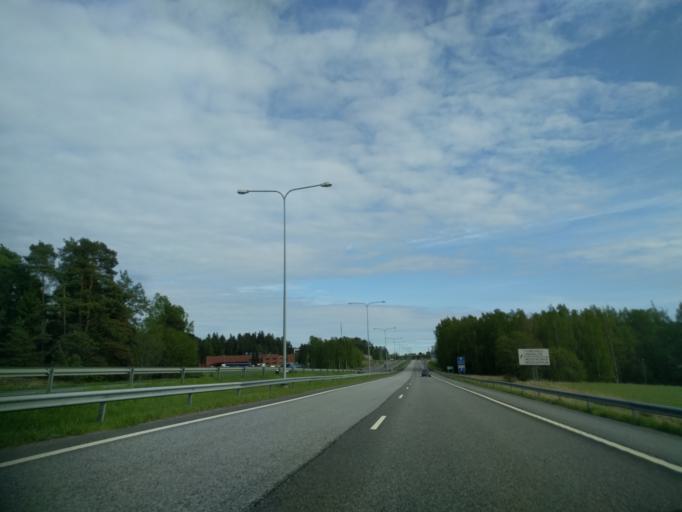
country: FI
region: Varsinais-Suomi
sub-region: Turku
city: Raisio
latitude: 60.4705
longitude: 22.1968
